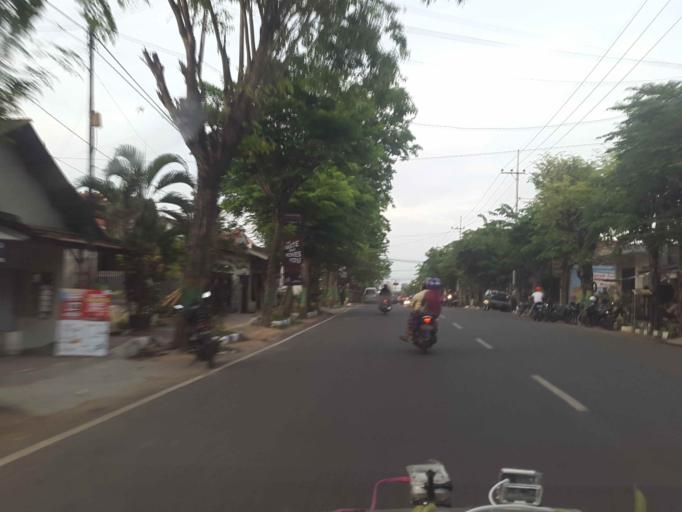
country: ID
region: East Java
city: Sumenep
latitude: -7.0202
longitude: 113.8572
